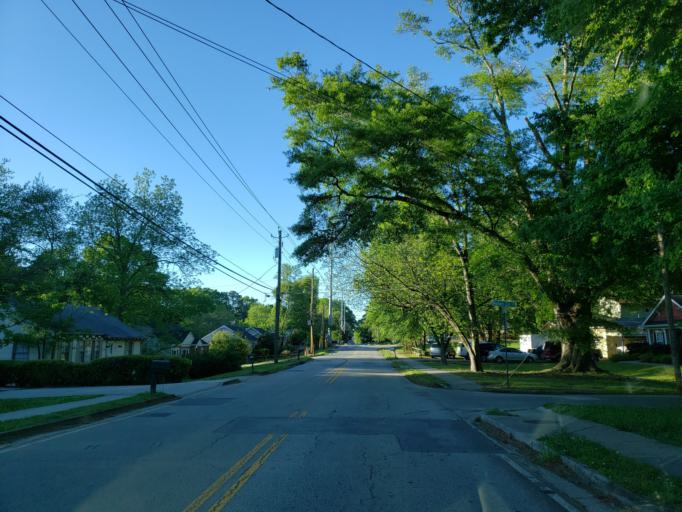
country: US
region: Georgia
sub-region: Cobb County
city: Fair Oaks
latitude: 33.9080
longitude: -84.5400
